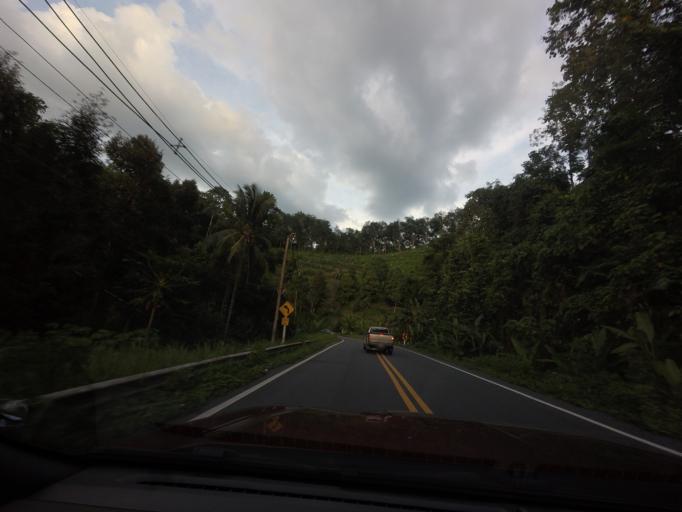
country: TH
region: Yala
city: Than To
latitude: 6.0387
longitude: 101.2077
